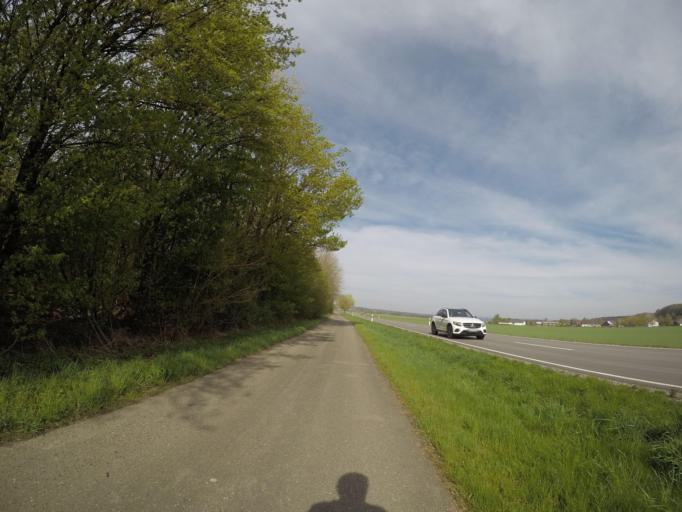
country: DE
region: Baden-Wuerttemberg
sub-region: Tuebingen Region
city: Saulgau
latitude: 48.0138
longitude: 9.5358
